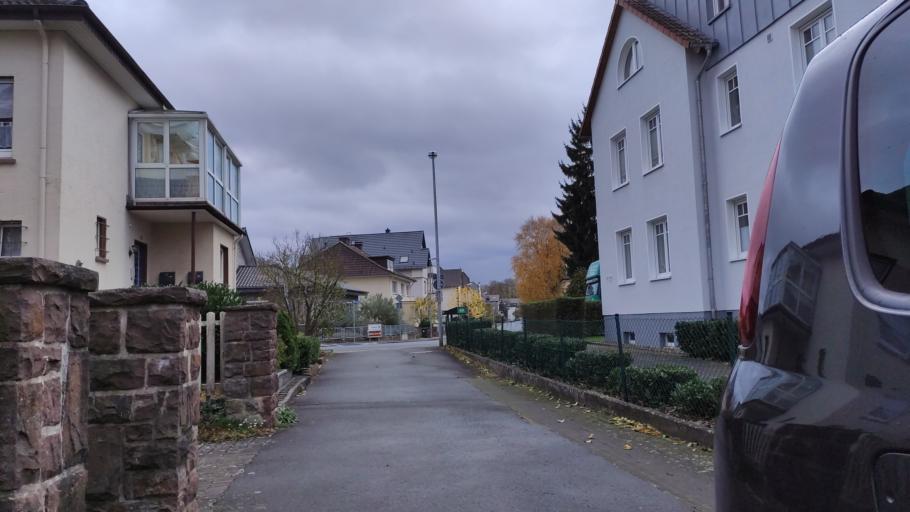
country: DE
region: North Rhine-Westphalia
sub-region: Regierungsbezirk Detmold
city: Hoexter
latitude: 51.7798
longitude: 9.3851
